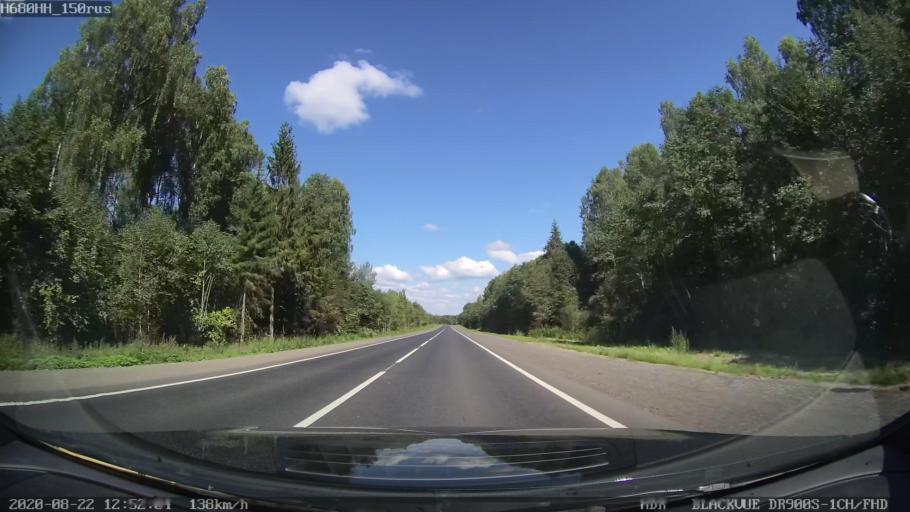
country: RU
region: Tverskaya
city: Rameshki
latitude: 57.4958
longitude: 36.2553
